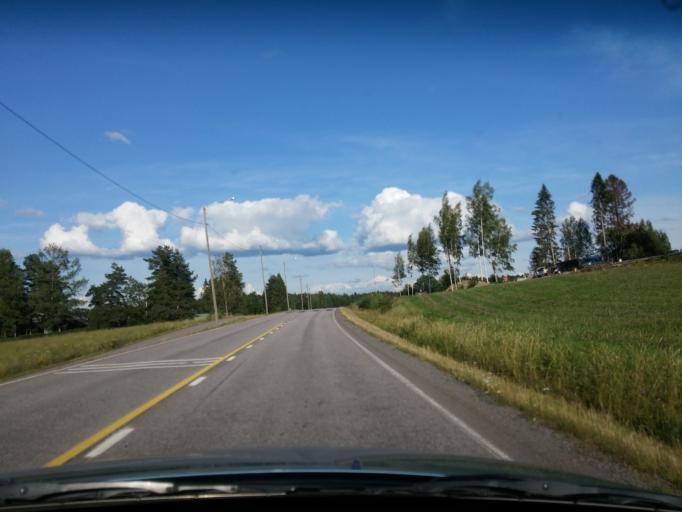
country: FI
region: Uusimaa
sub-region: Porvoo
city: Askola
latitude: 60.5261
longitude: 25.5879
